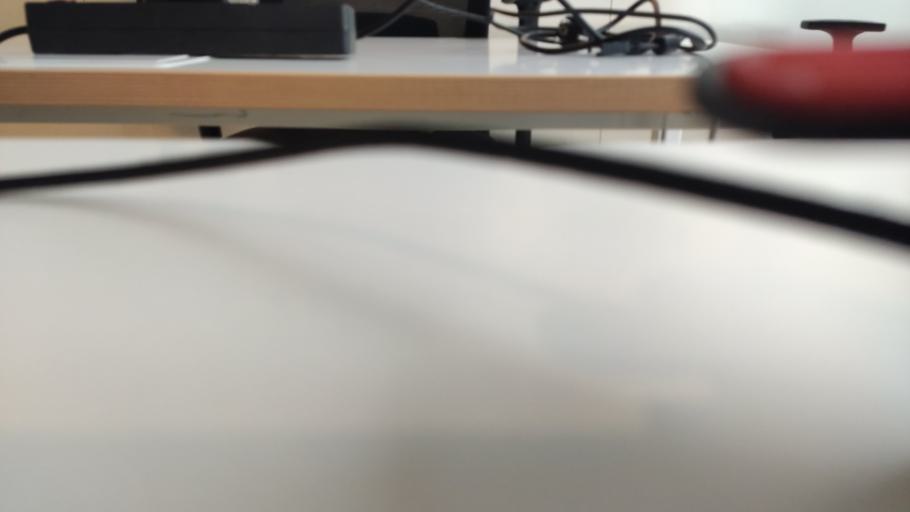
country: RU
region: Moskovskaya
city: Shevlyakovo
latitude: 56.4213
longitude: 36.9665
